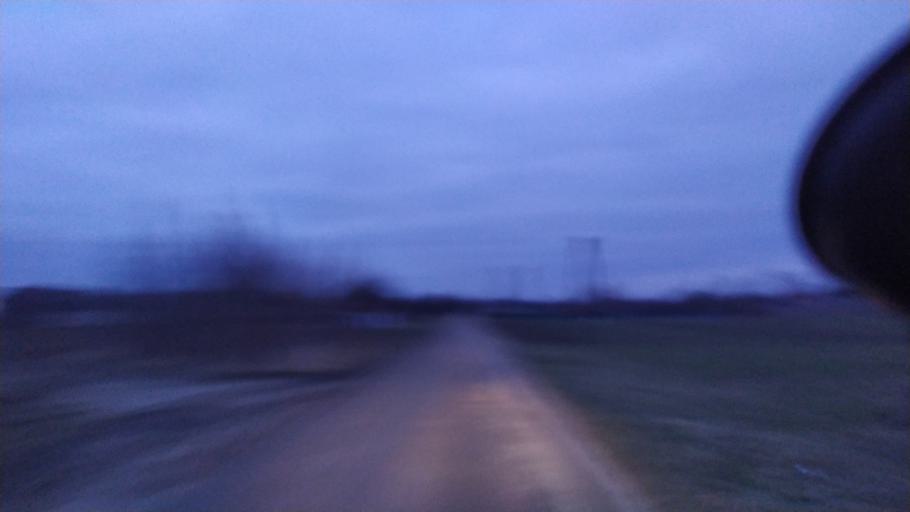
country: PL
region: Lublin Voivodeship
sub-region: Powiat lubartowski
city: Kamionka
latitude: 51.3945
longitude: 22.4178
